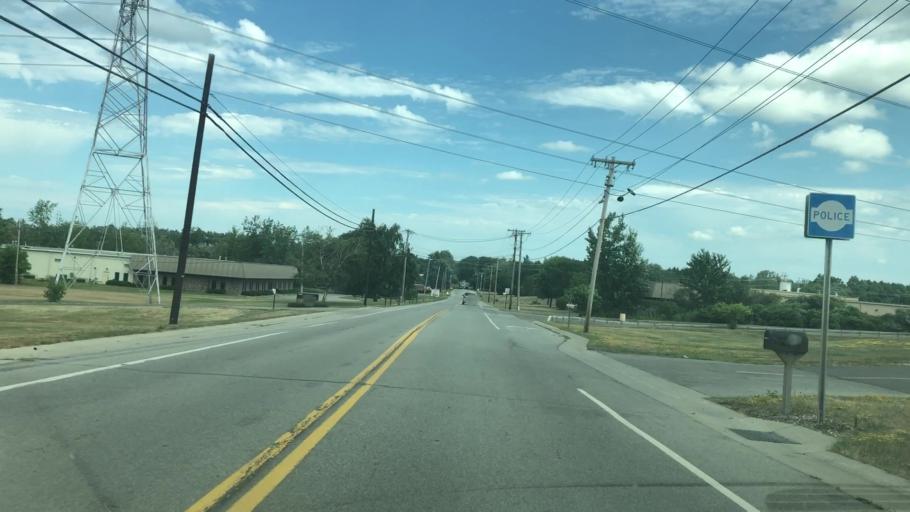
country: US
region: New York
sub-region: Wayne County
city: Macedon
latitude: 43.0664
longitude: -77.3611
